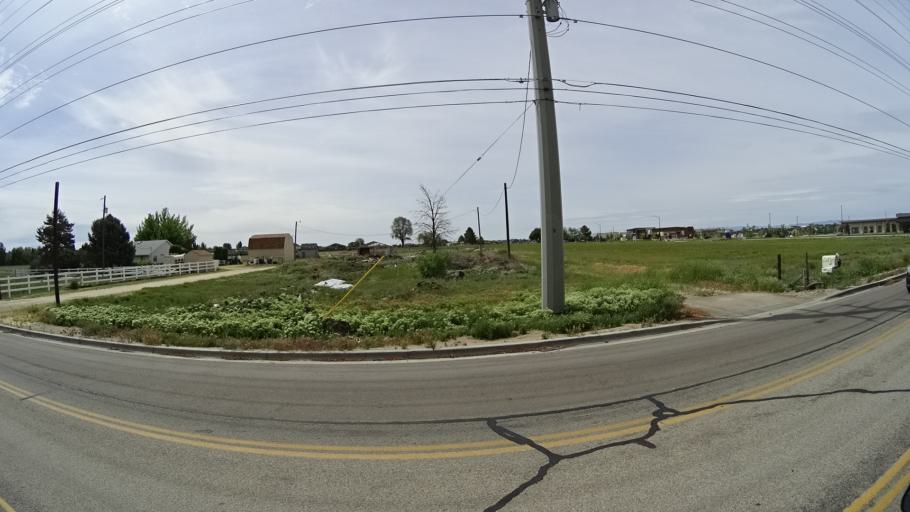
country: US
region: Idaho
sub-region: Ada County
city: Meridian
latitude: 43.5612
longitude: -116.3433
